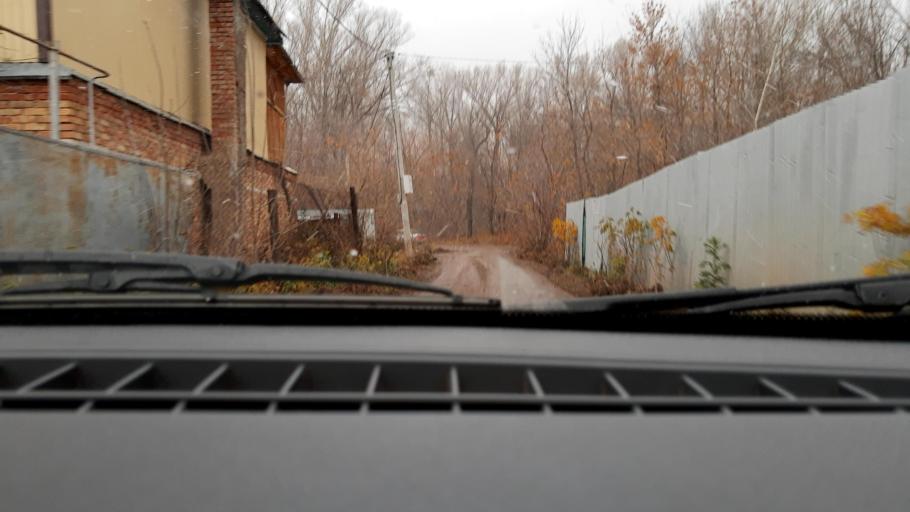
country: RU
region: Bashkortostan
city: Ufa
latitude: 54.7581
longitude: 55.9235
